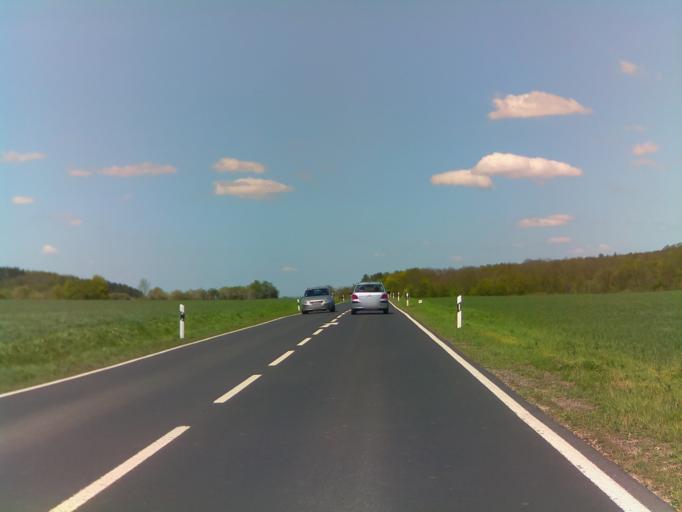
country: DE
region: Thuringia
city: Dornheim
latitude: 50.8055
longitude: 10.9792
